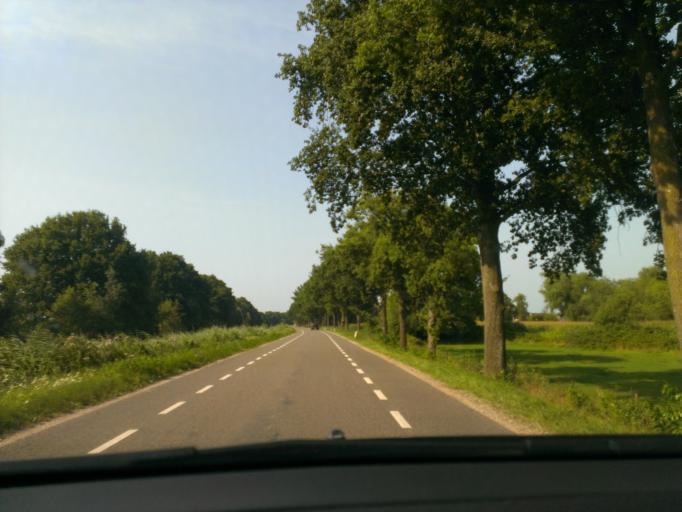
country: NL
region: Gelderland
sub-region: Gemeente Epe
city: Oene
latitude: 52.3483
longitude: 6.0245
